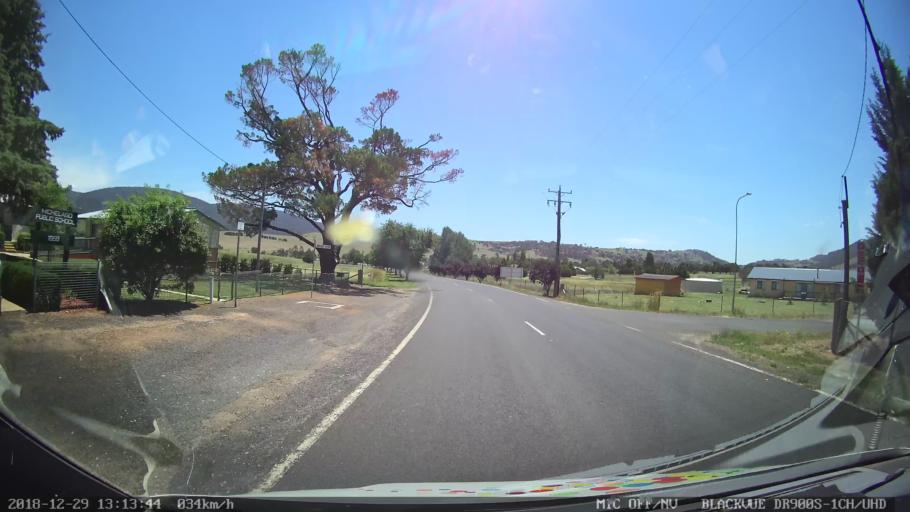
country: AU
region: Australian Capital Territory
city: Macarthur
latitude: -35.7057
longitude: 149.1621
